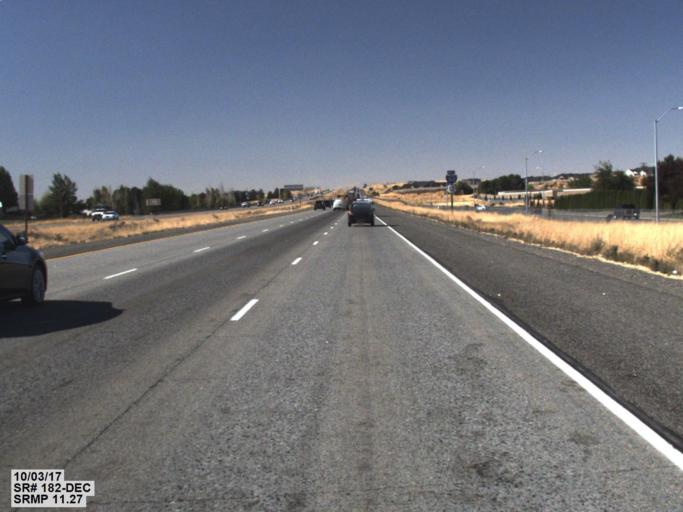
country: US
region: Washington
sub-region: Franklin County
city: West Pasco
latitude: 46.2544
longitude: -119.1453
